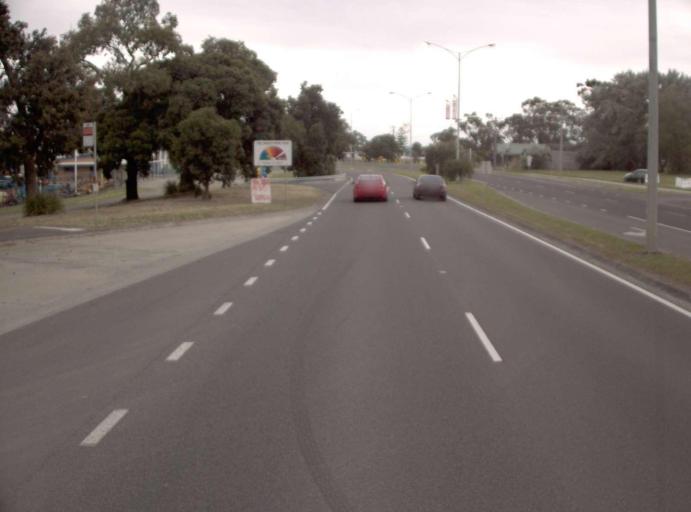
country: AU
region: Victoria
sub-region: Casey
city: Tooradin
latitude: -38.2104
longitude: 145.3775
